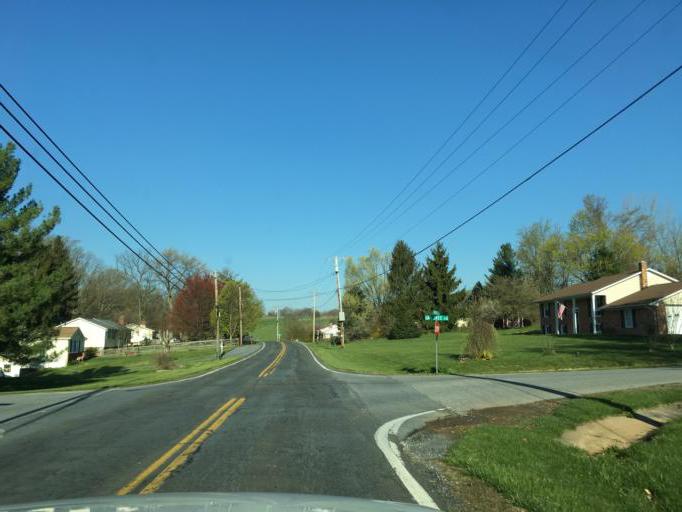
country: US
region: Maryland
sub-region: Frederick County
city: Linganore
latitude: 39.4870
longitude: -77.2606
